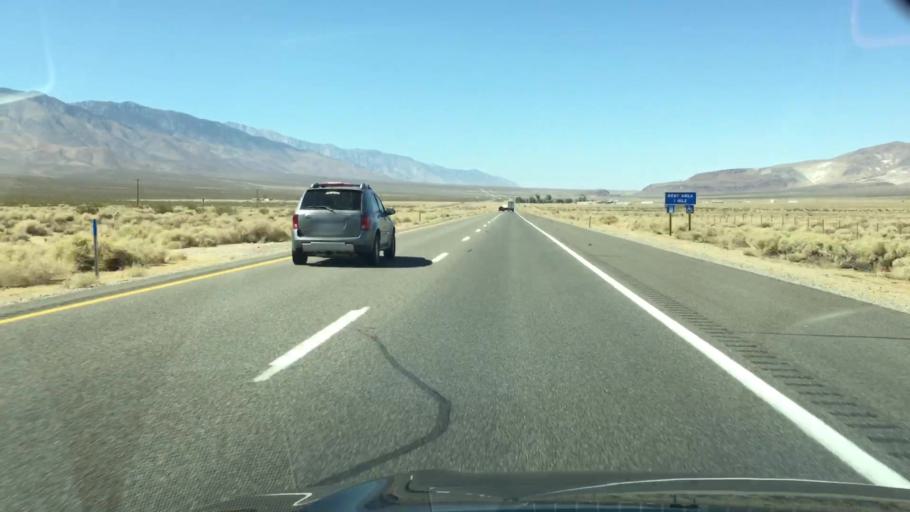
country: US
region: California
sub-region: Kern County
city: Inyokern
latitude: 36.0318
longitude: -117.9427
